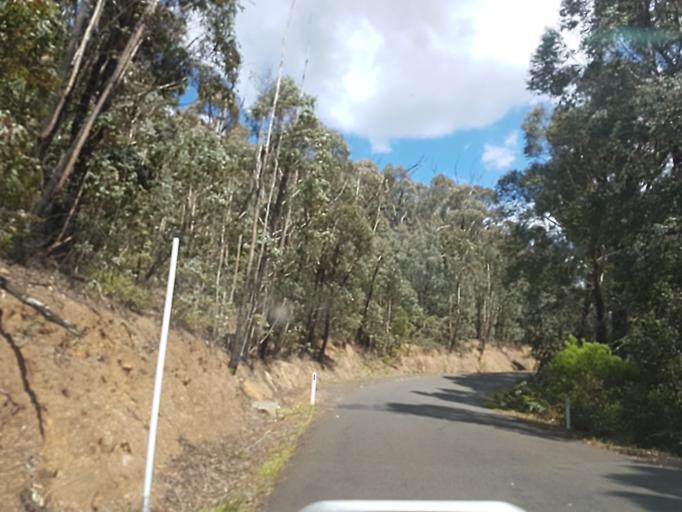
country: AU
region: Victoria
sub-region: East Gippsland
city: Bairnsdale
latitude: -37.3900
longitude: 147.2382
